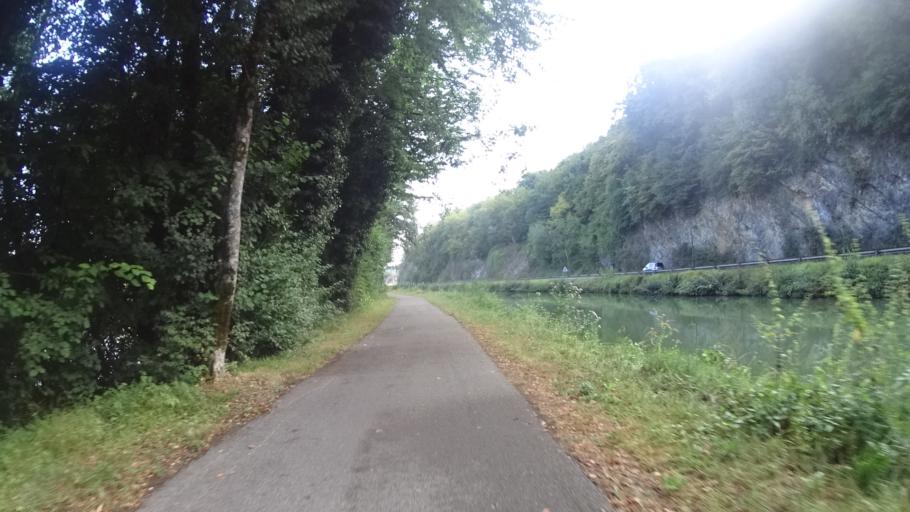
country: FR
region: Franche-Comte
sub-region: Departement du Doubs
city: Boussieres
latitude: 47.1526
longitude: 5.8556
